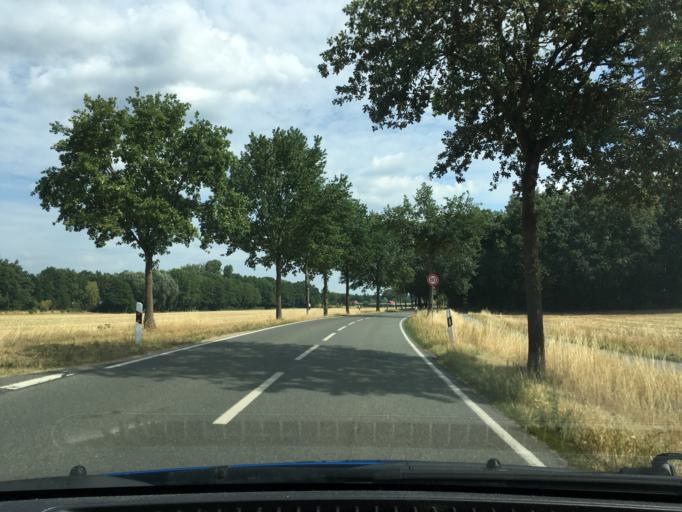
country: DE
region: Lower Saxony
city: Karwitz
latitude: 53.1241
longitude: 10.9544
